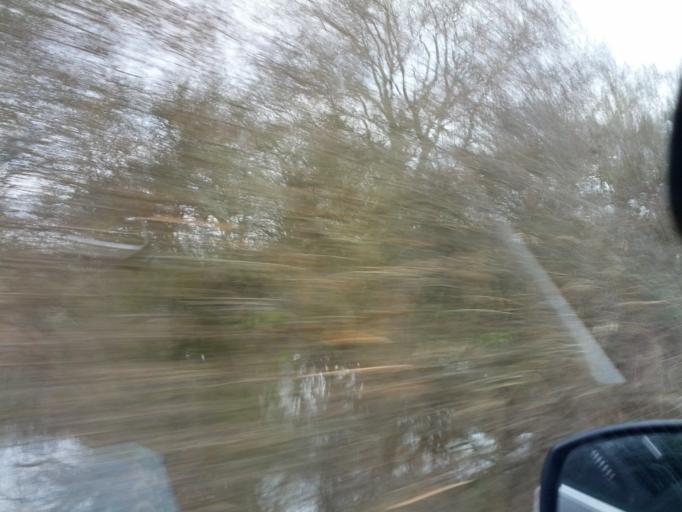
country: IE
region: Connaught
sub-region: County Galway
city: Gort
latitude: 53.1534
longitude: -8.8600
